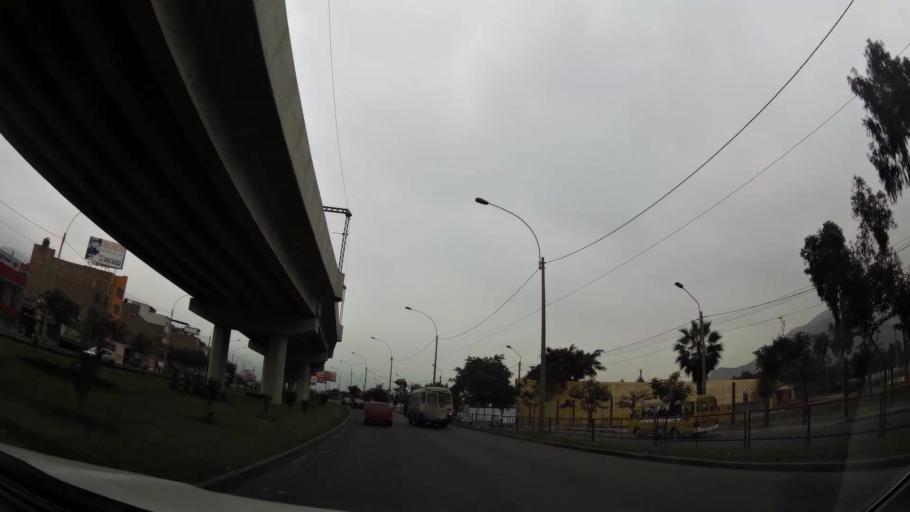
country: PE
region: Lima
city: Lima
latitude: -12.0120
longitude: -77.0021
